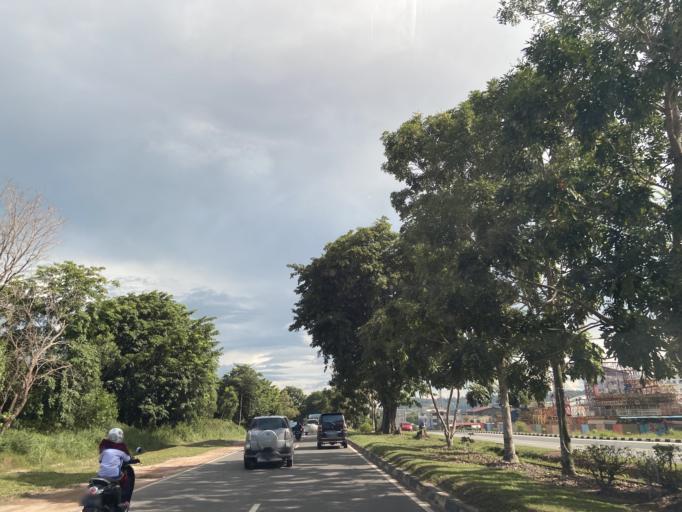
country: SG
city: Singapore
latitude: 1.1086
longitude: 104.0412
